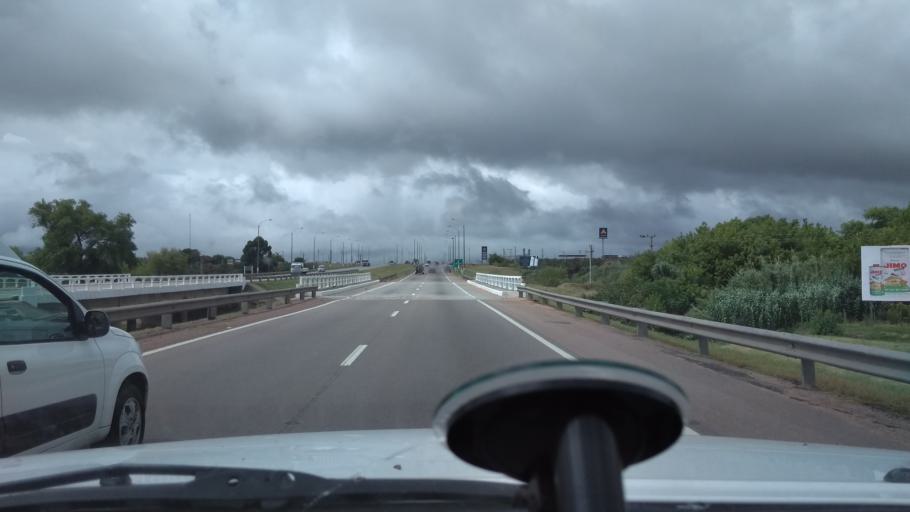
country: UY
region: Canelones
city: La Paz
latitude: -34.7545
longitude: -56.2578
